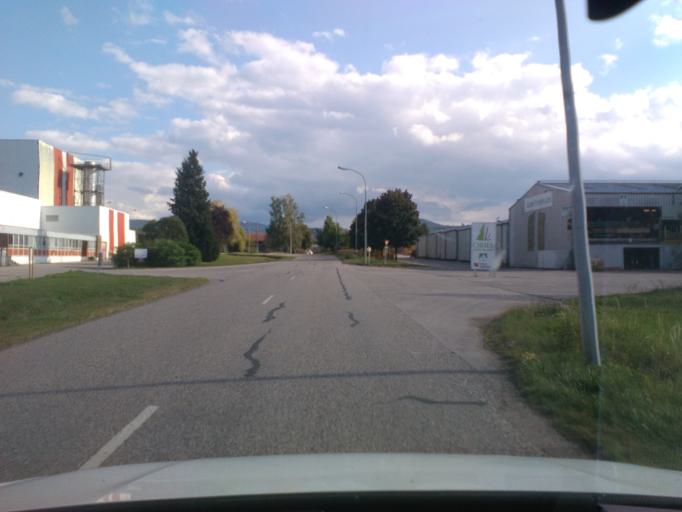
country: FR
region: Lorraine
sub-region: Departement des Vosges
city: Corcieux
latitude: 48.1846
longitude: 6.8828
